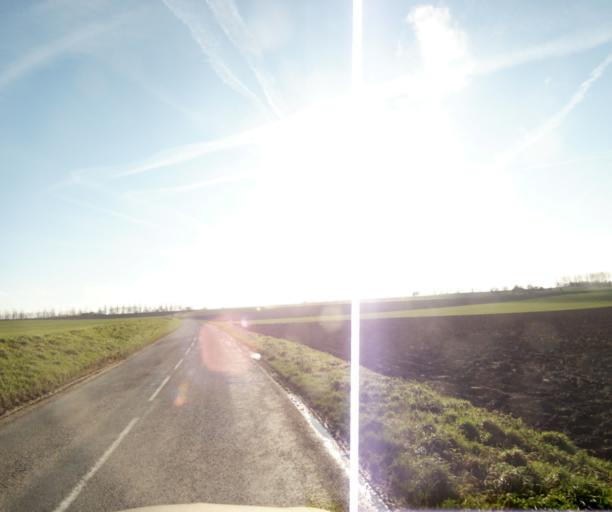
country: FR
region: Nord-Pas-de-Calais
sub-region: Departement du Nord
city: Saultain
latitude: 50.3262
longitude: 3.5746
